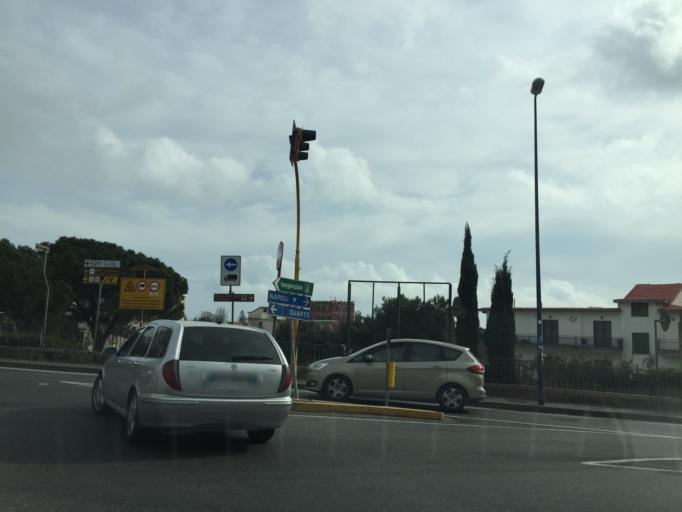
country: IT
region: Campania
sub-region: Provincia di Napoli
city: Pozzuoli
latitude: 40.8296
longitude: 14.1299
